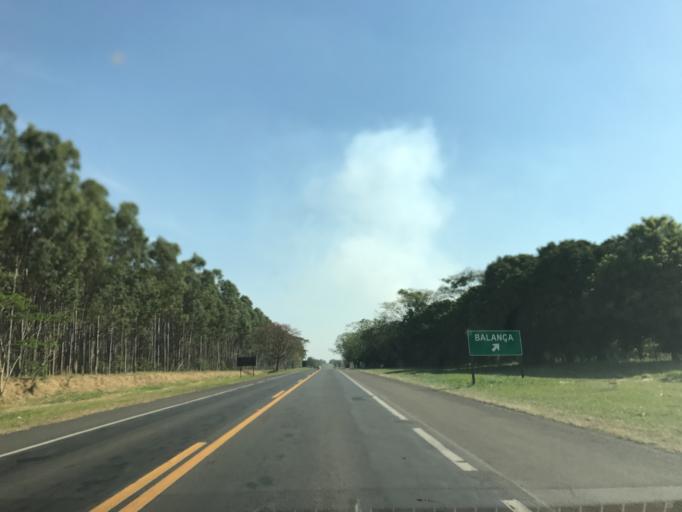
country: BR
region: Sao Paulo
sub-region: Penapolis
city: Penapolis
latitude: -21.3762
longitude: -50.0850
